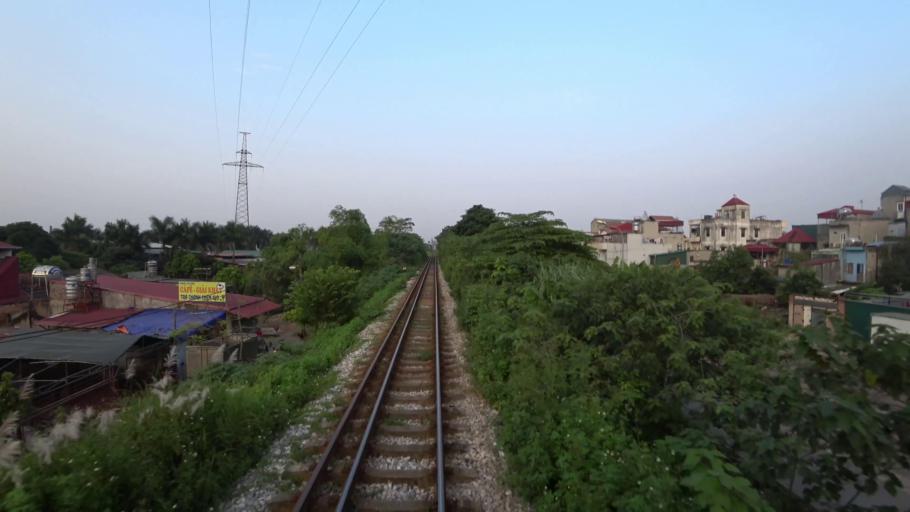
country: VN
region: Ha Noi
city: Trau Quy
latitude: 21.0888
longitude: 105.9191
